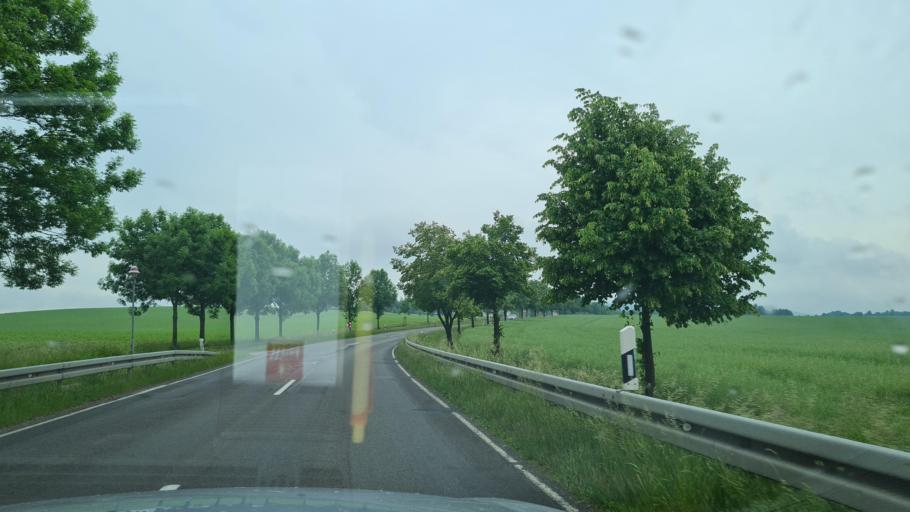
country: DE
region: Saxony
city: Kirschau
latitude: 51.0995
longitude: 14.4423
